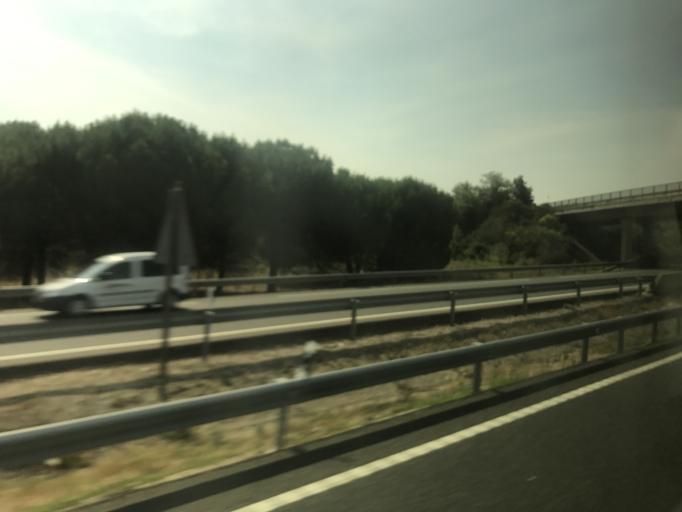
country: ES
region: Castille and Leon
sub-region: Provincia de Palencia
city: Quintana del Puente
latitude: 42.0900
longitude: -4.2099
